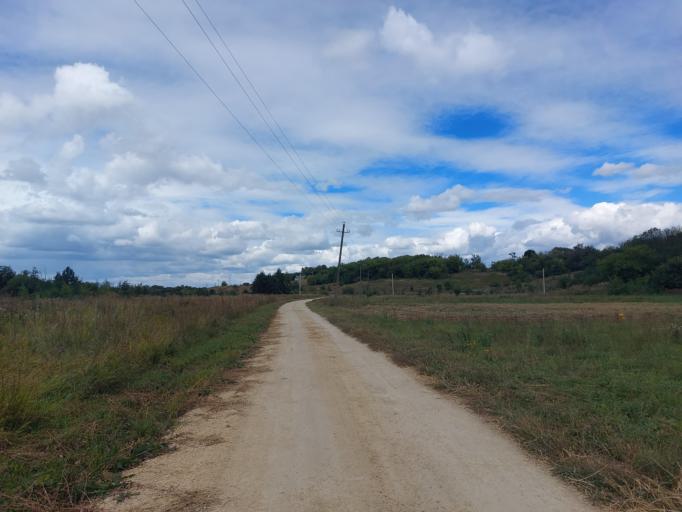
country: RU
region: Lipetsk
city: Terbuny
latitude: 52.2670
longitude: 38.2051
